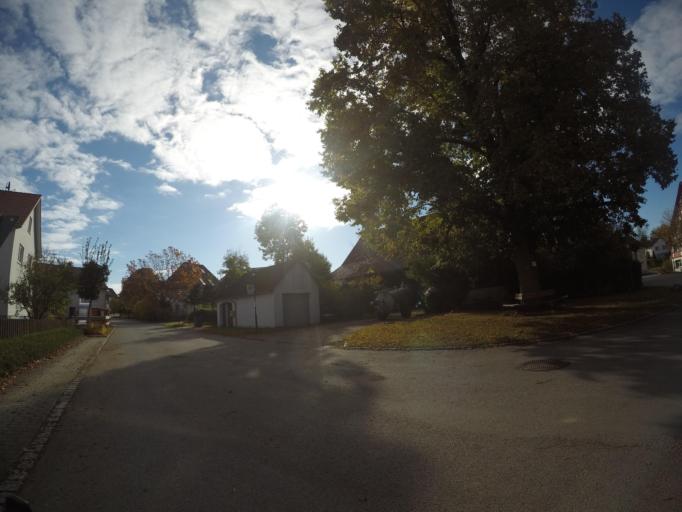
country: DE
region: Baden-Wuerttemberg
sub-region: Tuebingen Region
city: Herbertingen
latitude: 48.0490
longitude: 9.4509
